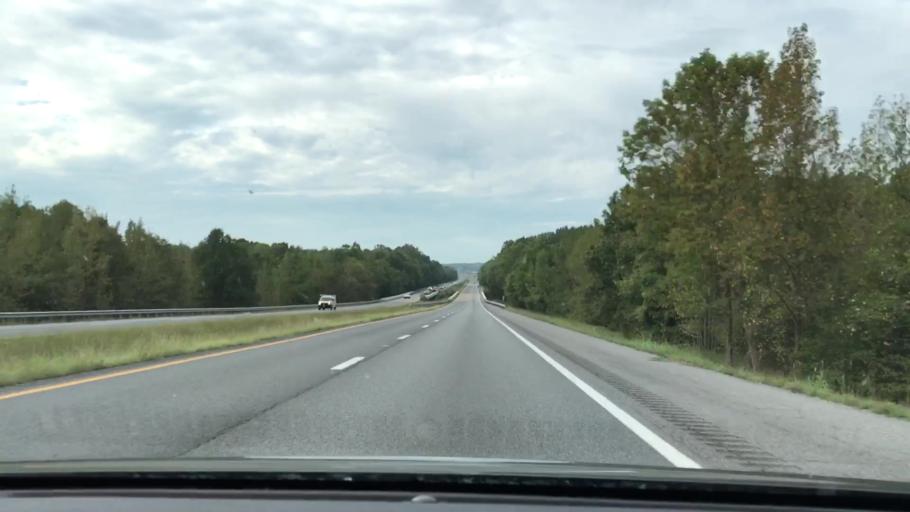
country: US
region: Kentucky
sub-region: Marshall County
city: Benton
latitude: 36.8888
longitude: -88.3529
